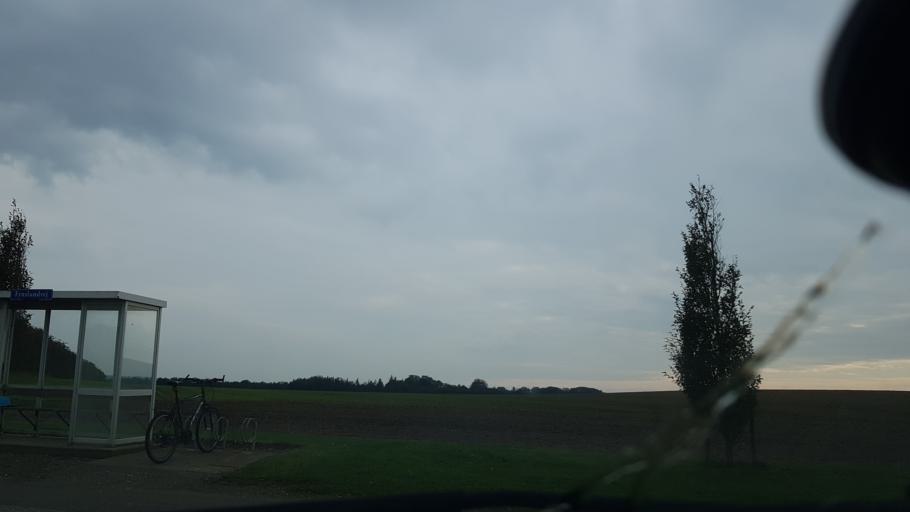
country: DK
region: South Denmark
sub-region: Kolding Kommune
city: Lunderskov
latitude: 55.5410
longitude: 9.3276
